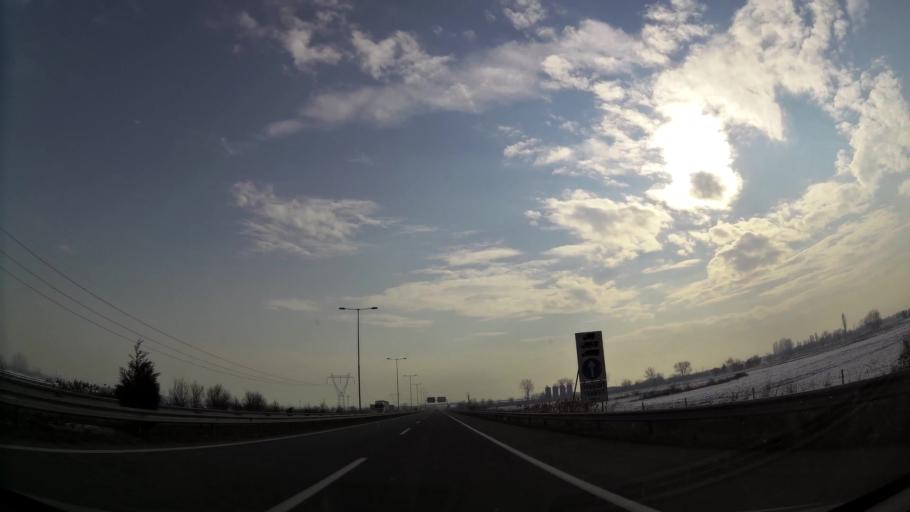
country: MK
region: Aracinovo
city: Arachinovo
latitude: 42.0241
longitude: 21.5316
